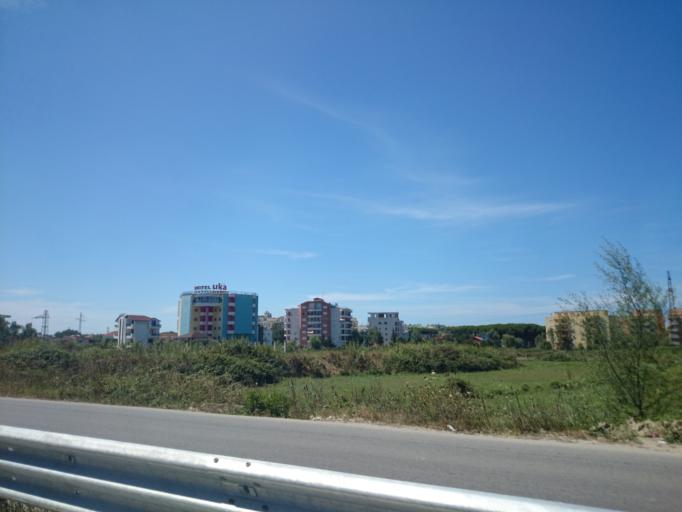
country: AL
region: Tirane
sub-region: Rrethi i Kavajes
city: Golem
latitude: 41.2343
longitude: 19.5239
